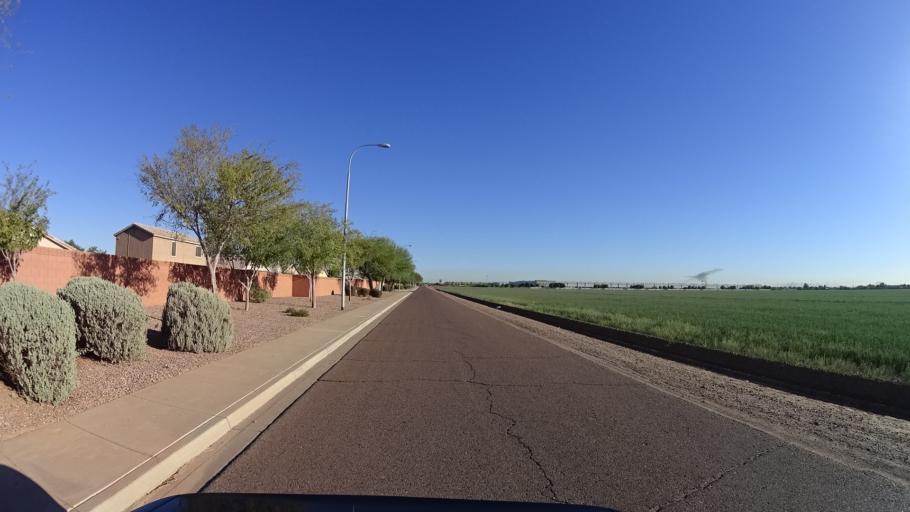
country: US
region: Arizona
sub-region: Maricopa County
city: Tolleson
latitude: 33.4268
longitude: -112.2126
